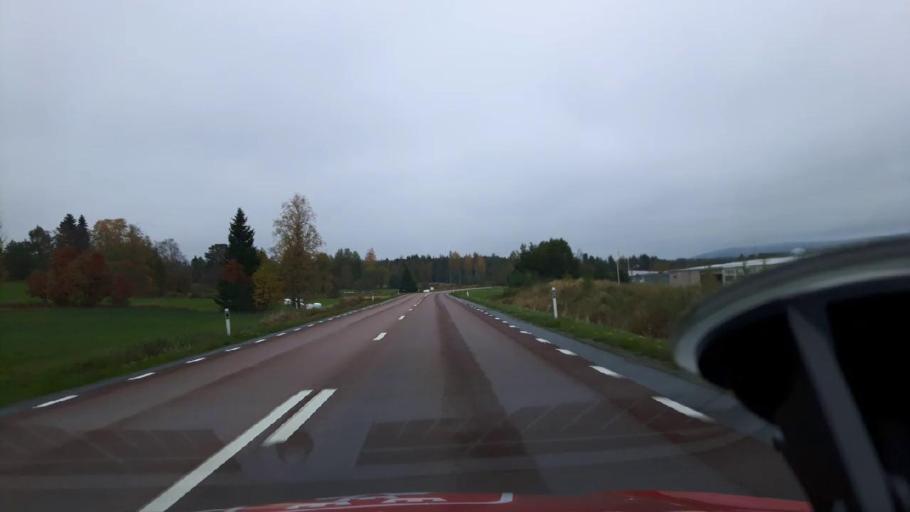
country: SE
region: Jaemtland
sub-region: Bergs Kommun
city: Hoverberg
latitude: 62.7614
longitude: 14.4373
